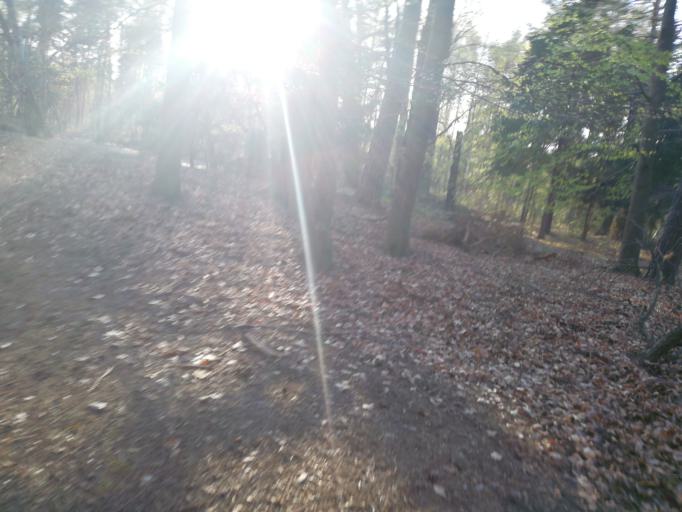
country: DE
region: Brandenburg
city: Calau
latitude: 51.7323
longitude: 13.9956
